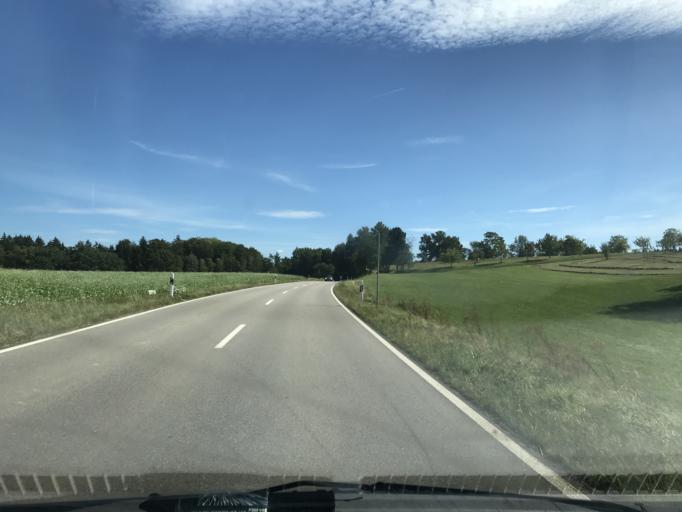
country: DE
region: Baden-Wuerttemberg
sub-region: Freiburg Region
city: Schopfheim
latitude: 47.6367
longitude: 7.8435
